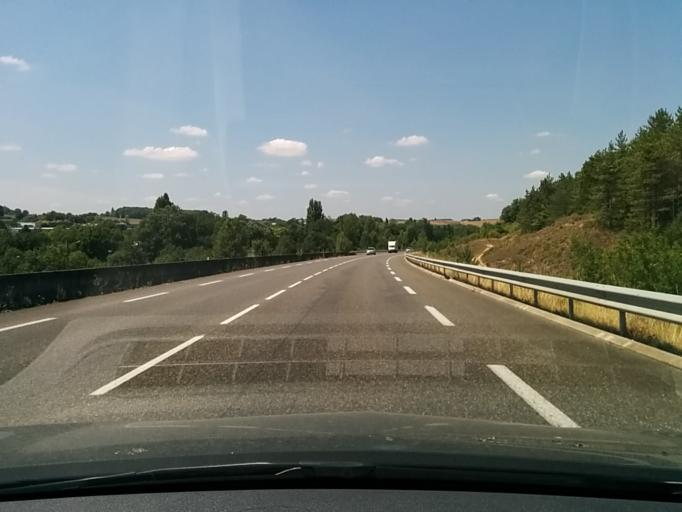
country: FR
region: Midi-Pyrenees
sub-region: Departement du Gers
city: Auch
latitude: 43.6605
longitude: 0.6289
